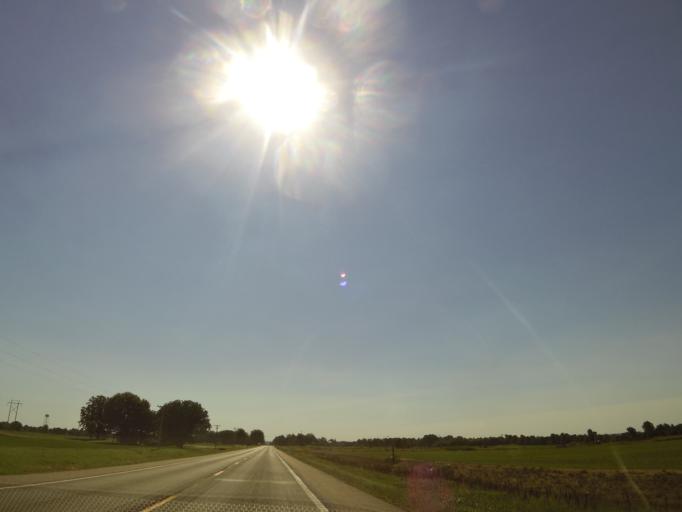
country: US
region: Arkansas
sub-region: Clay County
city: Corning
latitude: 36.4345
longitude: -90.4034
